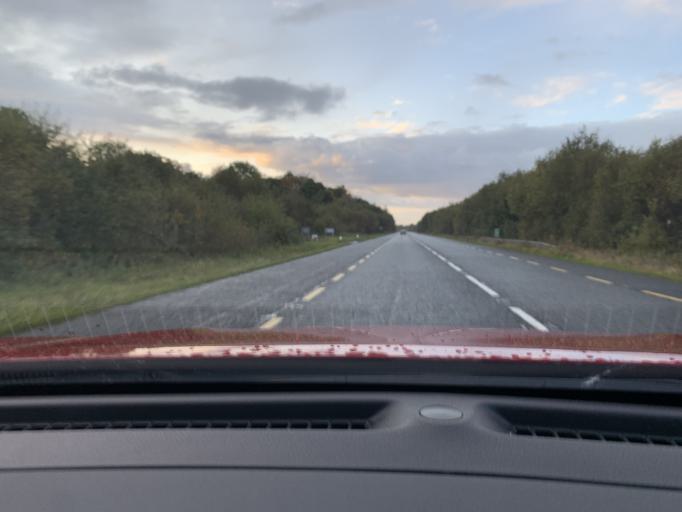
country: IE
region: Connaught
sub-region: County Leitrim
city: Carrick-on-Shannon
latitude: 53.9514
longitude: -8.1513
